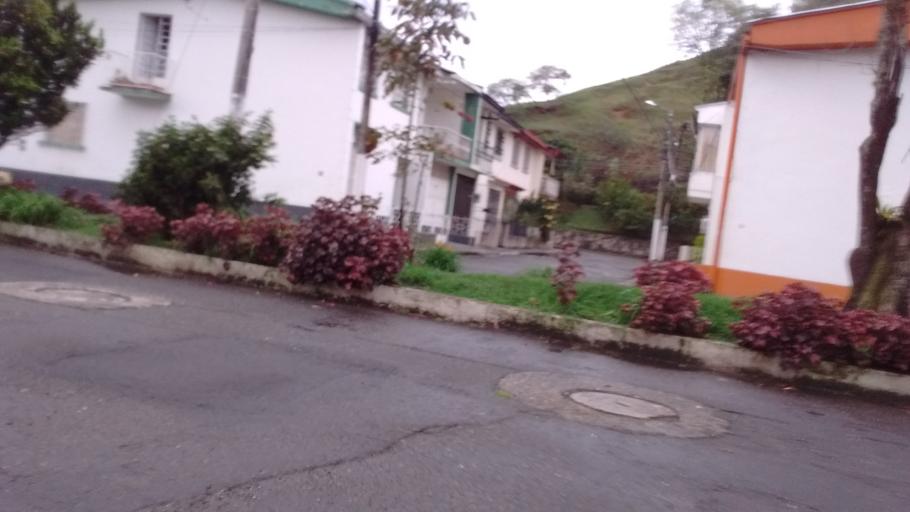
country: CO
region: Cauca
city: Popayan
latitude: 2.4435
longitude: -76.6009
